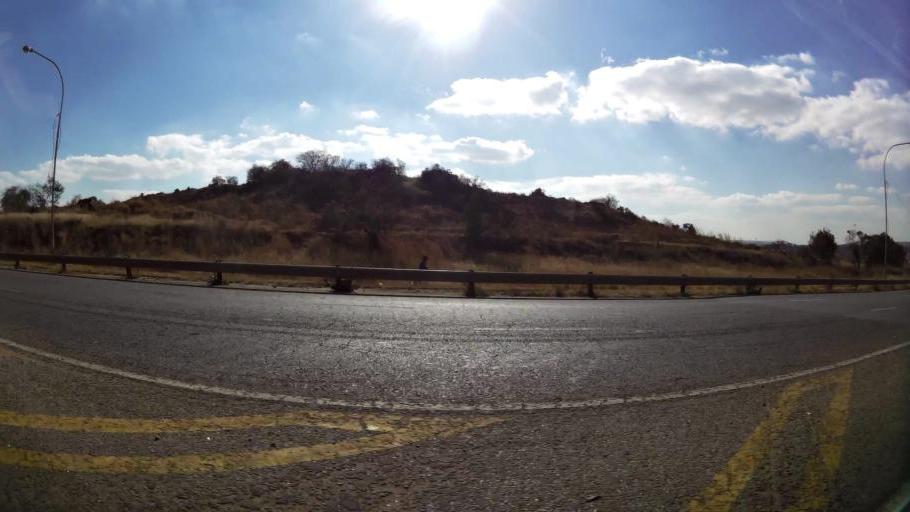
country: ZA
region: Gauteng
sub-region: City of Johannesburg Metropolitan Municipality
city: Soweto
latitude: -26.2783
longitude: 27.9424
